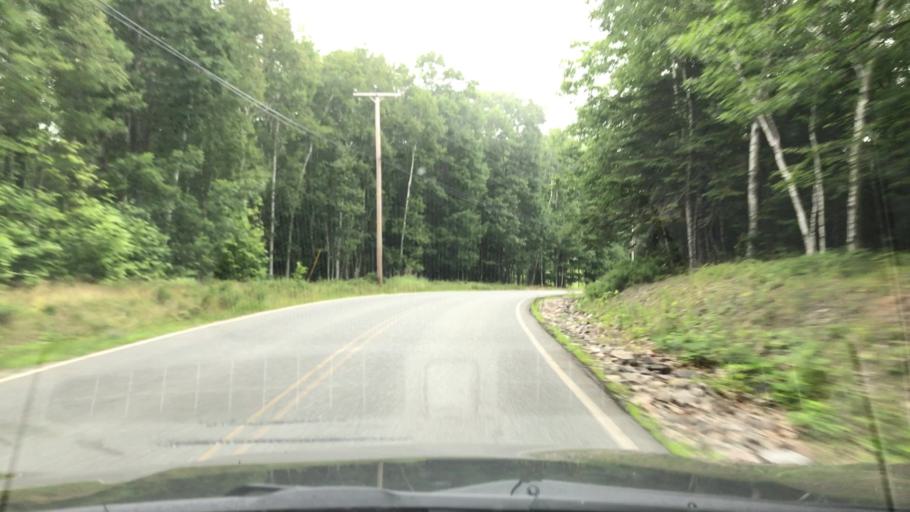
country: US
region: Maine
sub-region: Hancock County
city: Bar Harbor
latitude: 44.3410
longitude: -68.1805
